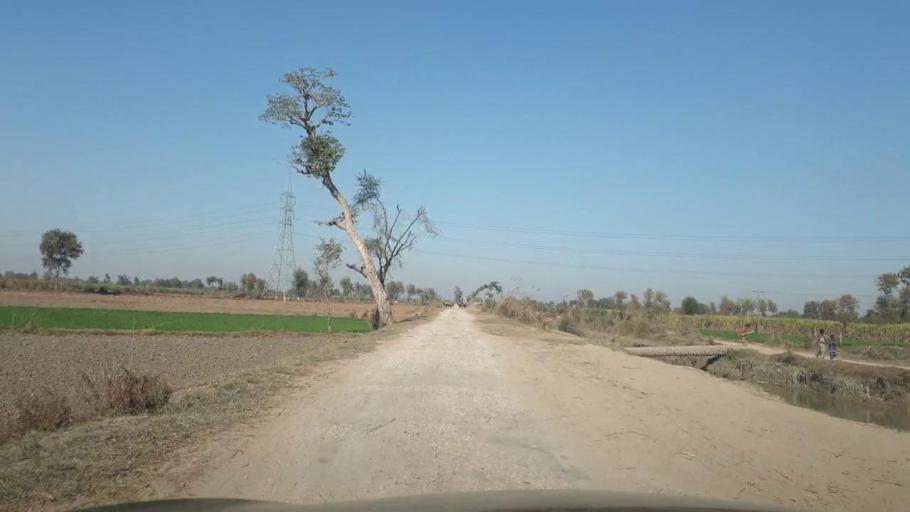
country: PK
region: Sindh
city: Ghotki
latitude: 27.9901
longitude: 69.4278
